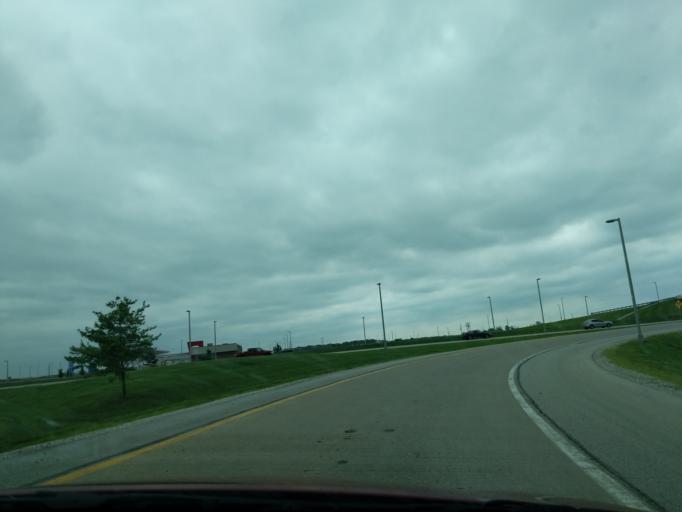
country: US
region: Indiana
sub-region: Hendricks County
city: Plainfield
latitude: 39.7012
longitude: -86.3170
